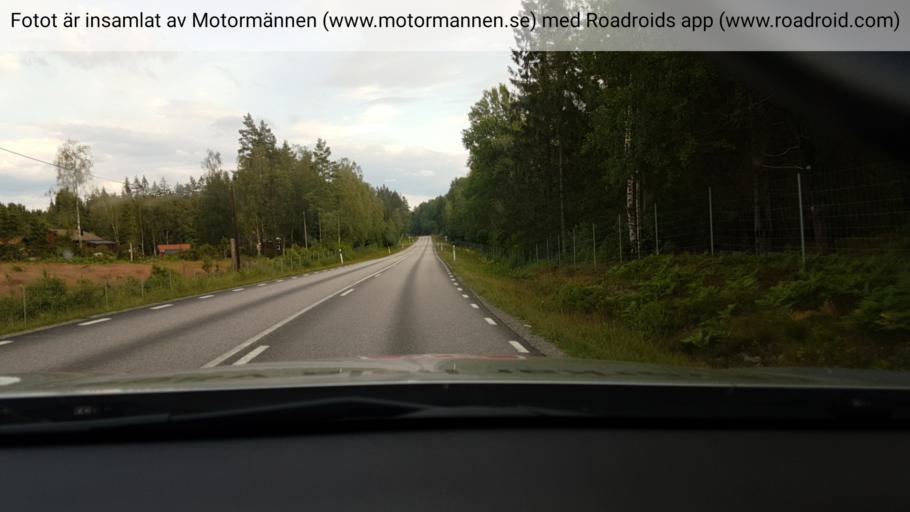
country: SE
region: Vaestra Goetaland
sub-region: Fargelanda Kommun
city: Faergelanda
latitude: 58.4735
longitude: 12.0144
